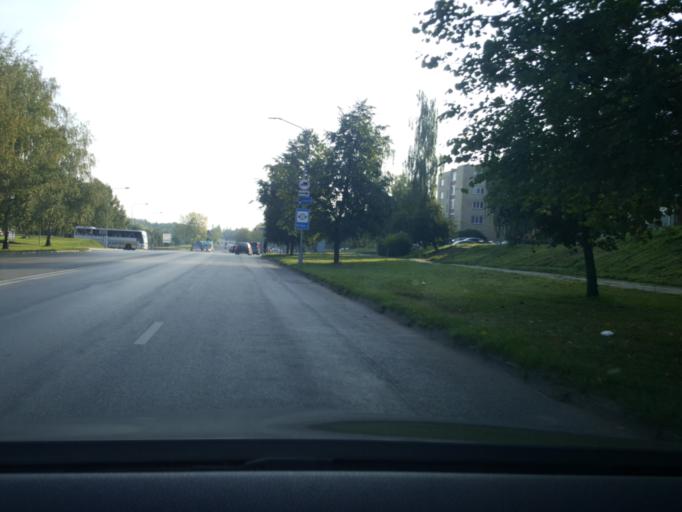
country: LT
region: Alytaus apskritis
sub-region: Alytus
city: Alytus
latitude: 54.4113
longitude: 24.0096
